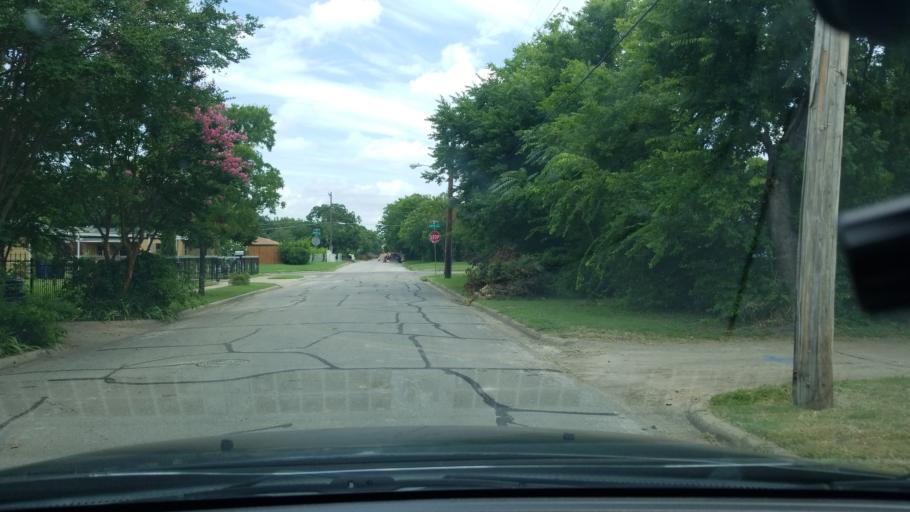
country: US
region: Texas
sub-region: Dallas County
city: Mesquite
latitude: 32.8228
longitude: -96.6745
